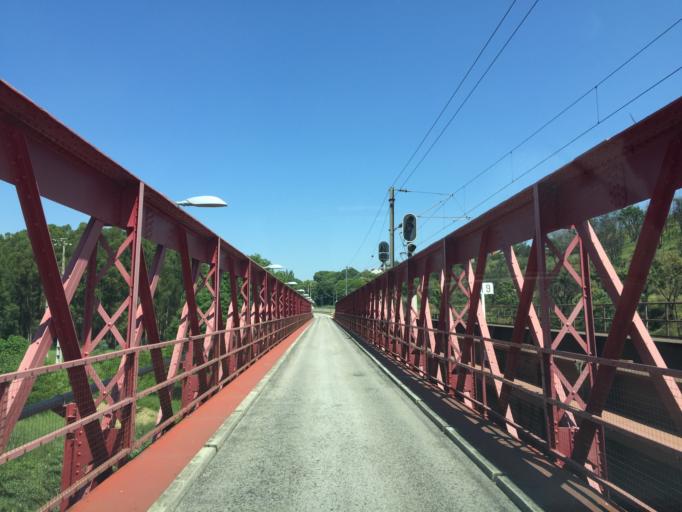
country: PT
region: Santarem
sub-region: Constancia
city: Constancia
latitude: 39.4685
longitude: -8.3409
